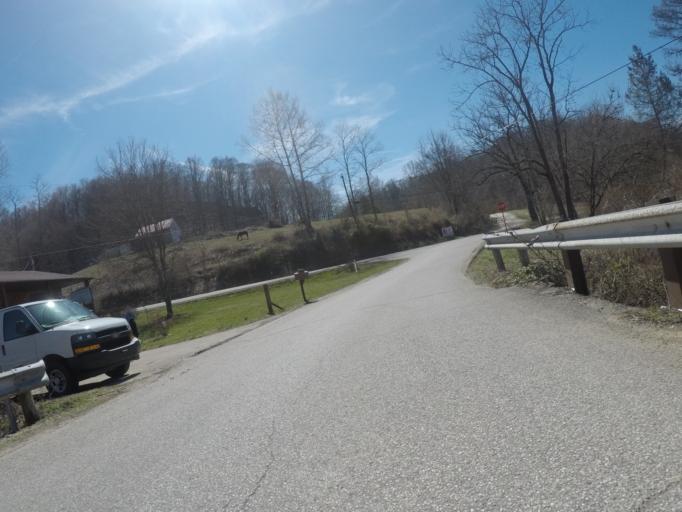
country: US
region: Ohio
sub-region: Lawrence County
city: South Point
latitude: 38.4660
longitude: -82.5689
